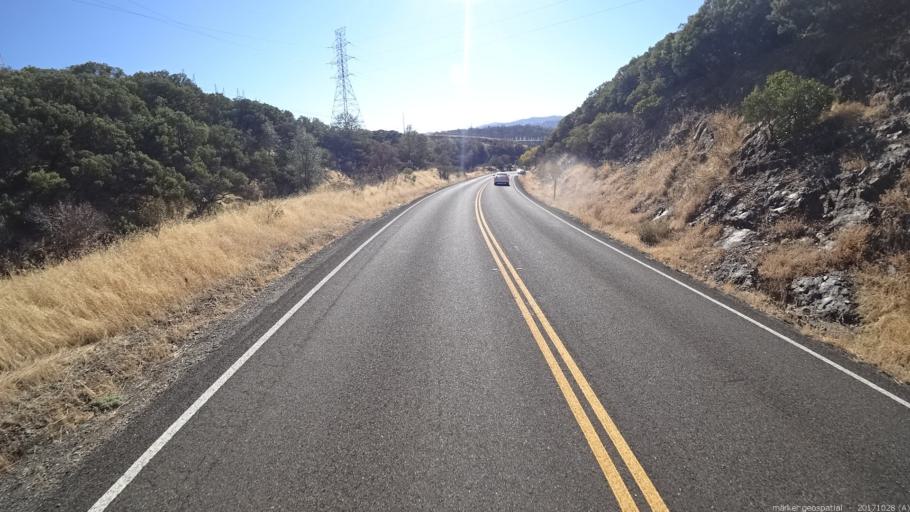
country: US
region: California
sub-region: Shasta County
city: Shasta
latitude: 40.6122
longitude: -122.4419
